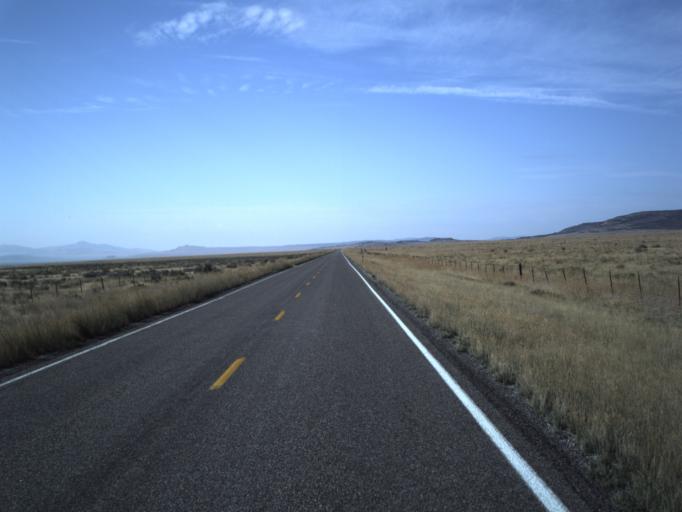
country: US
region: Idaho
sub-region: Oneida County
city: Malad City
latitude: 41.8964
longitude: -113.1088
